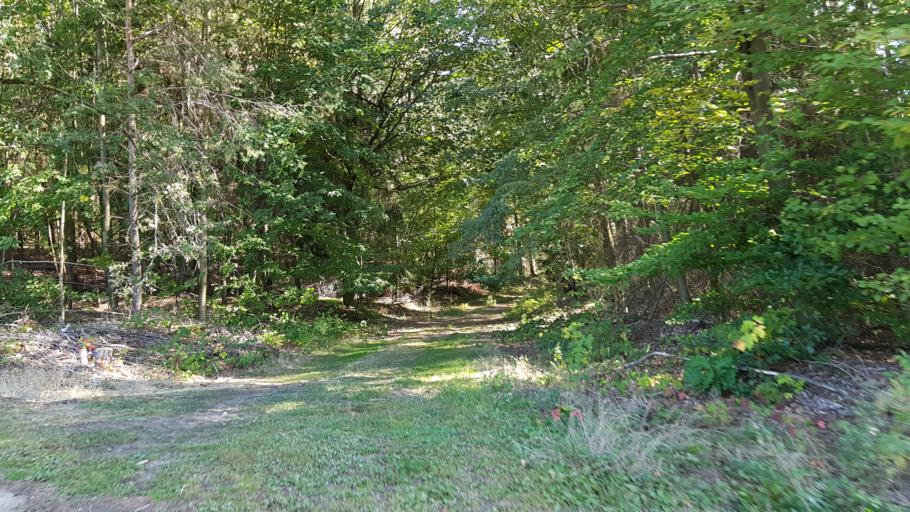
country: DE
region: Saxony
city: Grossnaundorf
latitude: 51.2191
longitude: 13.9493
